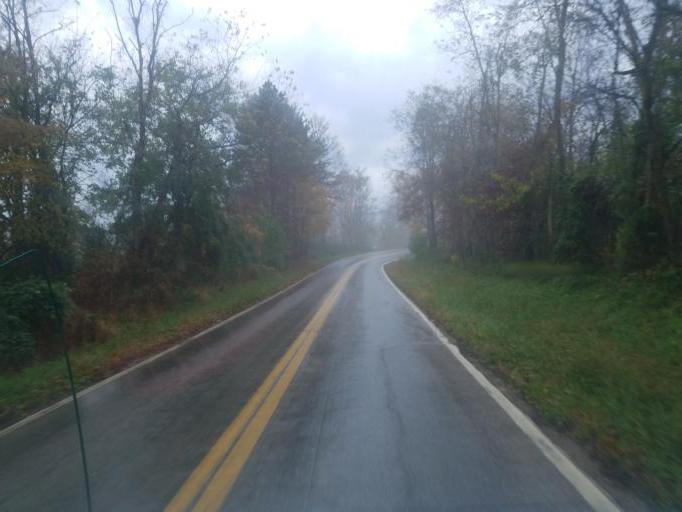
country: US
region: Ohio
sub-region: Morgan County
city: McConnelsville
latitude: 39.4900
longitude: -81.8803
